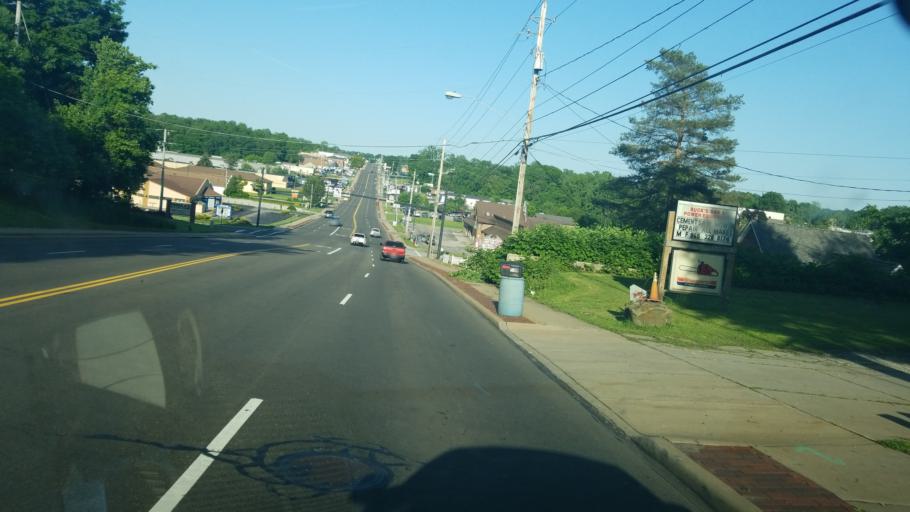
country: US
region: Ohio
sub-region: Summit County
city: Tallmadge
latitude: 41.1018
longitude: -81.4628
